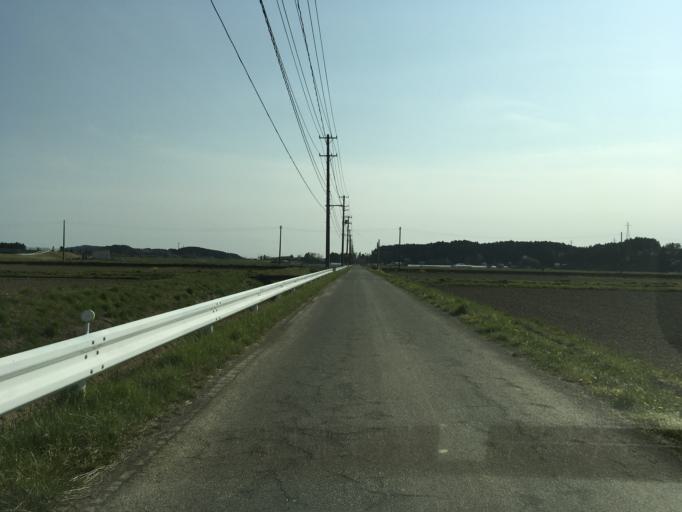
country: JP
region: Miyagi
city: Wakuya
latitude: 38.7298
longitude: 141.2907
